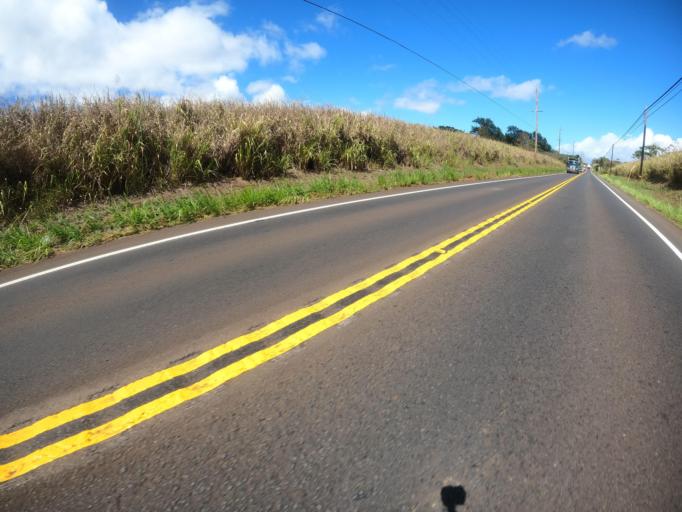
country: US
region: Hawaii
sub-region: Honolulu County
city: Schofield Barracks
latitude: 21.4533
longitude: -158.0598
